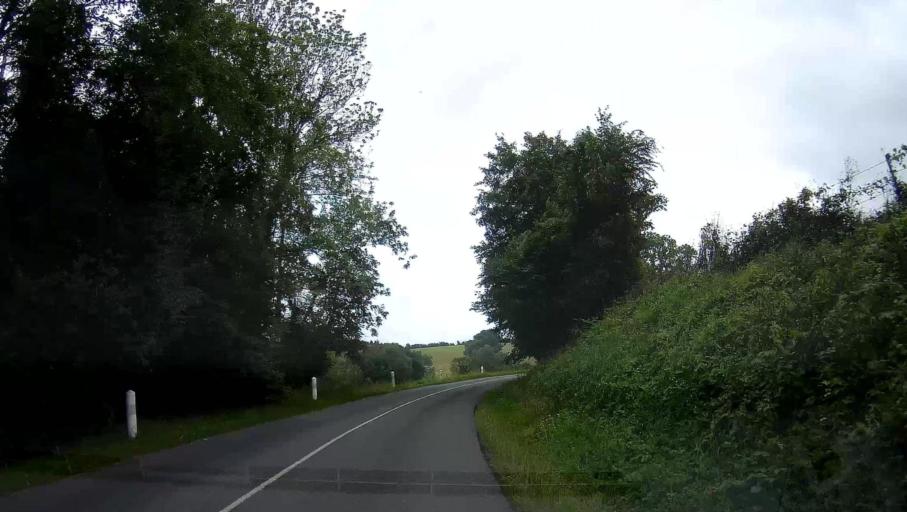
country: FR
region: Champagne-Ardenne
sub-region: Departement des Ardennes
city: Chateau-Porcien
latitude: 49.6298
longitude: 4.2400
